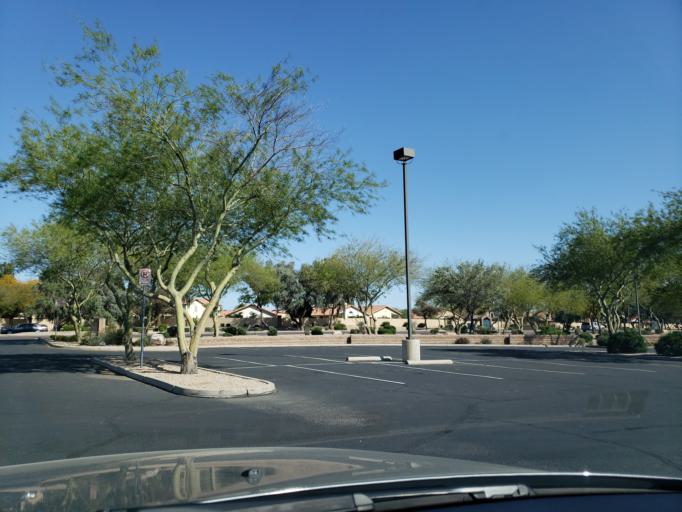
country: US
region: Arizona
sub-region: Maricopa County
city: Glendale
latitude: 33.5793
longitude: -112.1868
